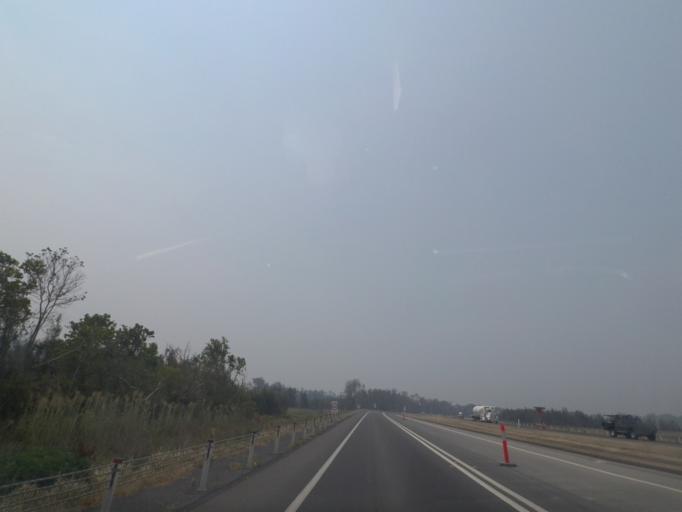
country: AU
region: New South Wales
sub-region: Ballina
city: Ballina
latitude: -28.8714
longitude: 153.4907
